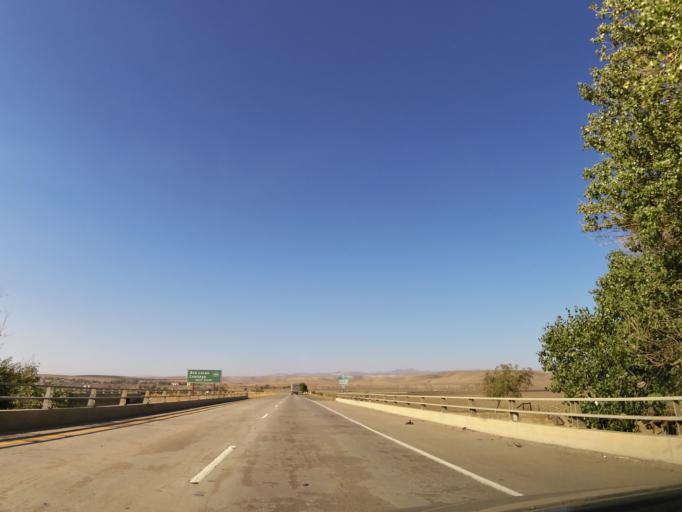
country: US
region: California
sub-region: Monterey County
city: King City
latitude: 36.1086
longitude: -121.0216
